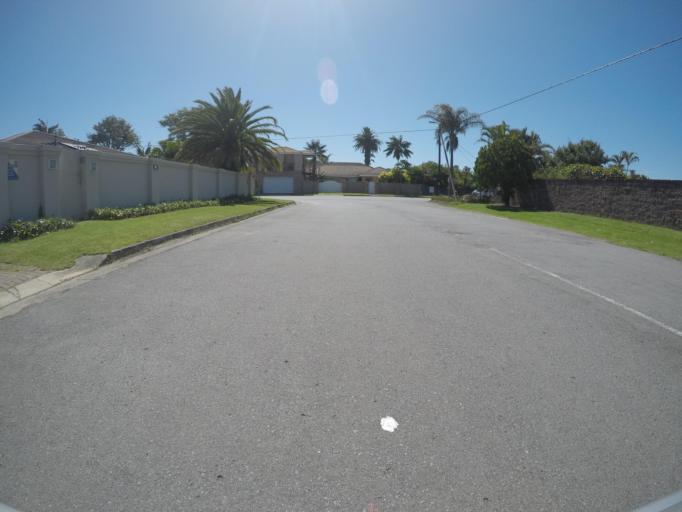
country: ZA
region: Eastern Cape
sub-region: Buffalo City Metropolitan Municipality
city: East London
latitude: -32.9846
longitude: 27.9296
